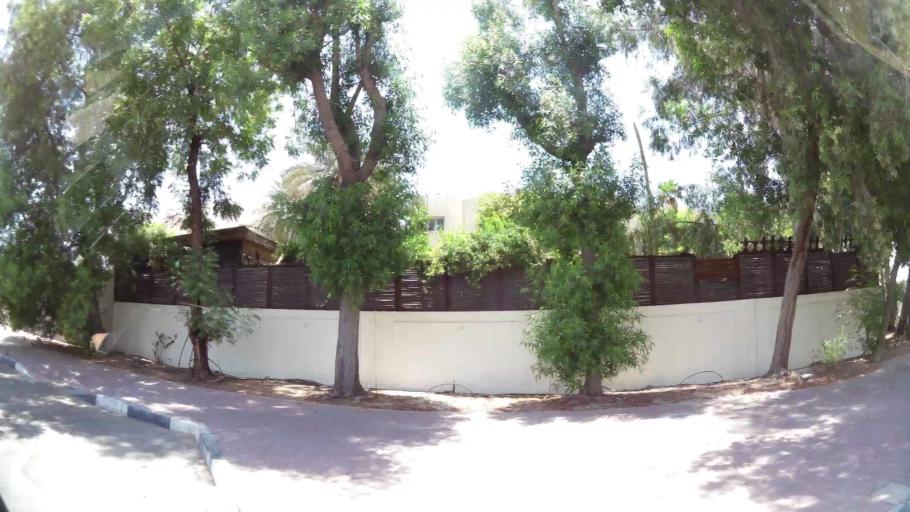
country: AE
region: Dubai
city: Dubai
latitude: 25.2150
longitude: 55.2561
